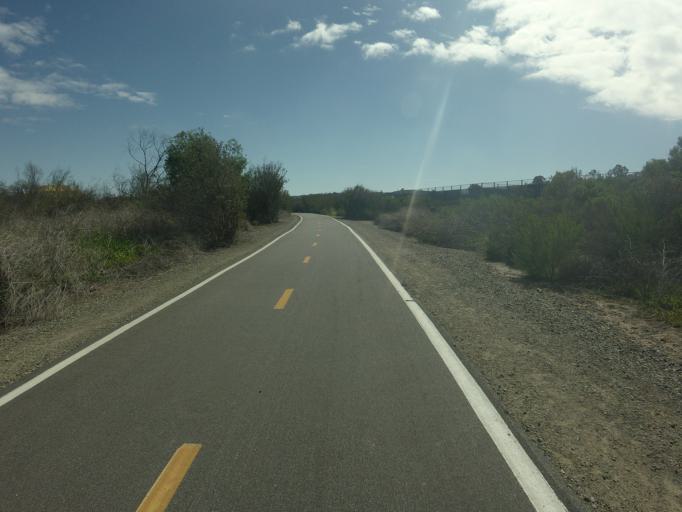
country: US
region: California
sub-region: Orange County
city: Aliso Viejo
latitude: 33.5634
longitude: -117.7184
